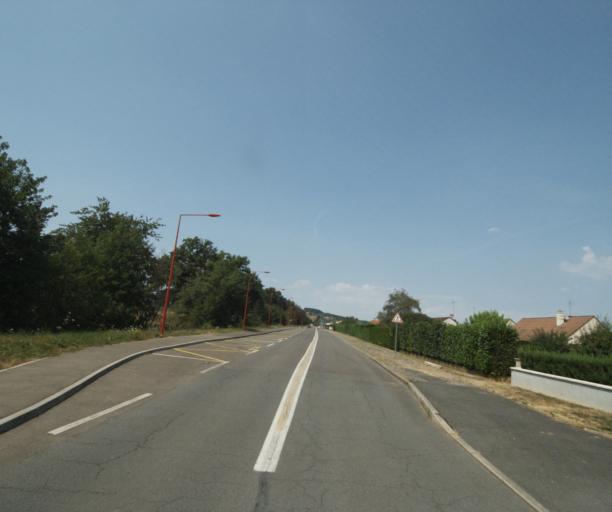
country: FR
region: Bourgogne
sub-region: Departement de Saone-et-Loire
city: Gueugnon
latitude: 46.6016
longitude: 4.0492
